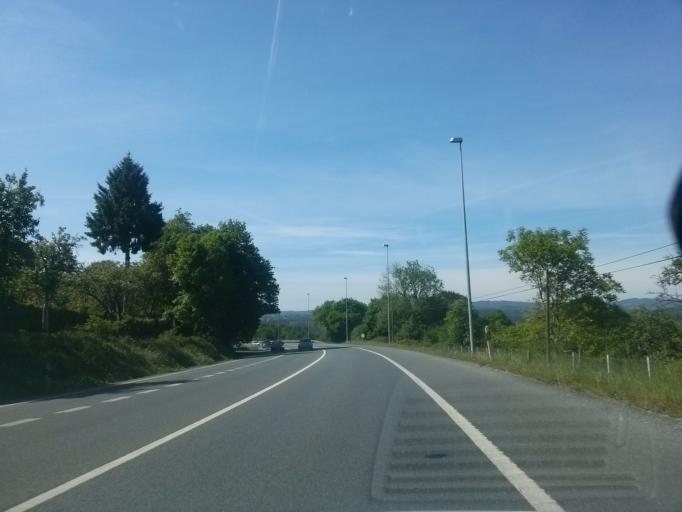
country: ES
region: Galicia
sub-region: Provincia de Lugo
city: Lugo
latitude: 43.0189
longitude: -7.5826
